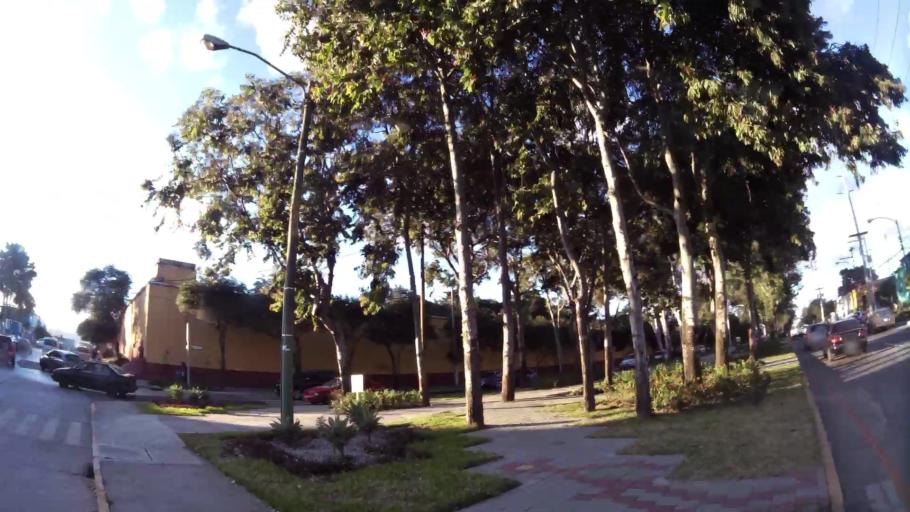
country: GT
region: Guatemala
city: Guatemala City
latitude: 14.6258
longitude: -90.5275
